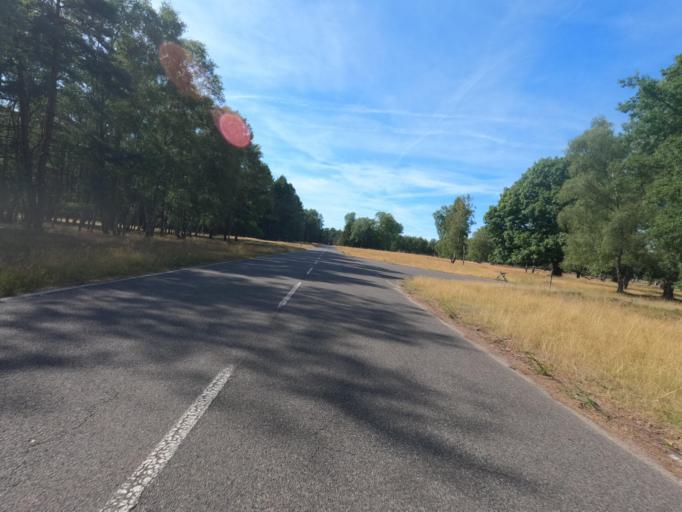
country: DE
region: North Rhine-Westphalia
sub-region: Regierungsbezirk Dusseldorf
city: Bruggen
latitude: 51.2648
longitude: 6.1482
